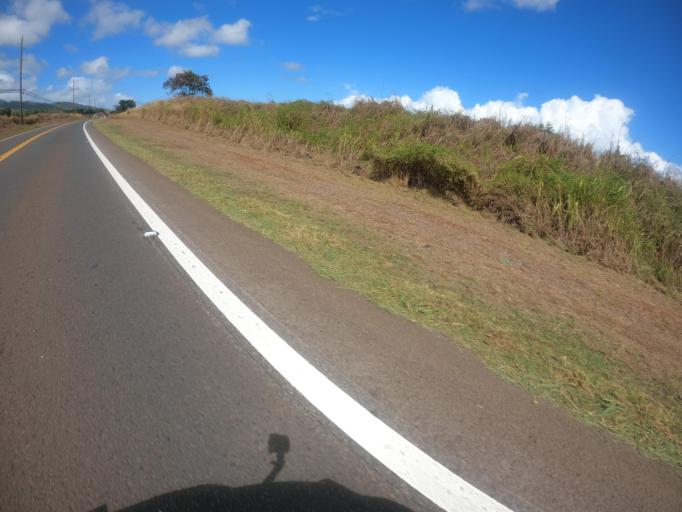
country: US
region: Hawaii
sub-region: Honolulu County
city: Village Park
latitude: 21.4272
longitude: -158.0548
